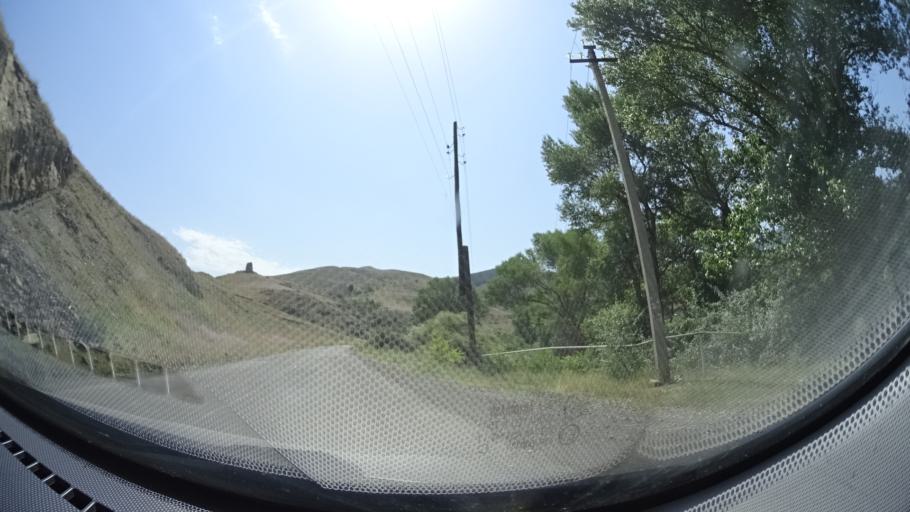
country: GE
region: Samtskhe-Javakheti
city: Aspindza
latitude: 41.6154
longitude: 43.1365
